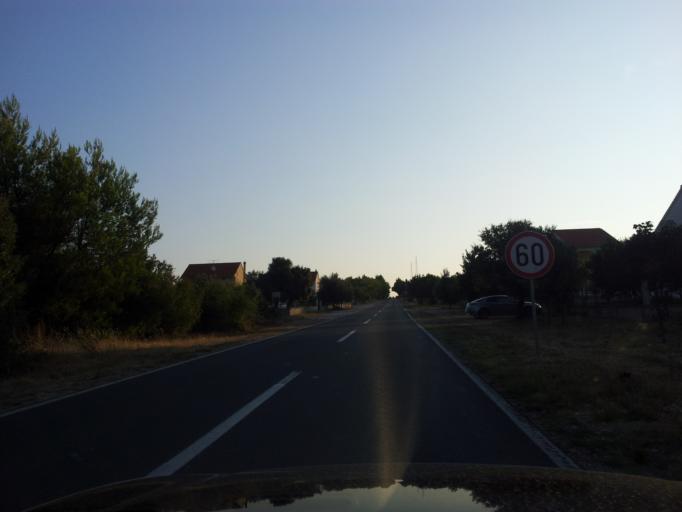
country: HR
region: Zadarska
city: Polaca
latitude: 43.9938
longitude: 15.4924
